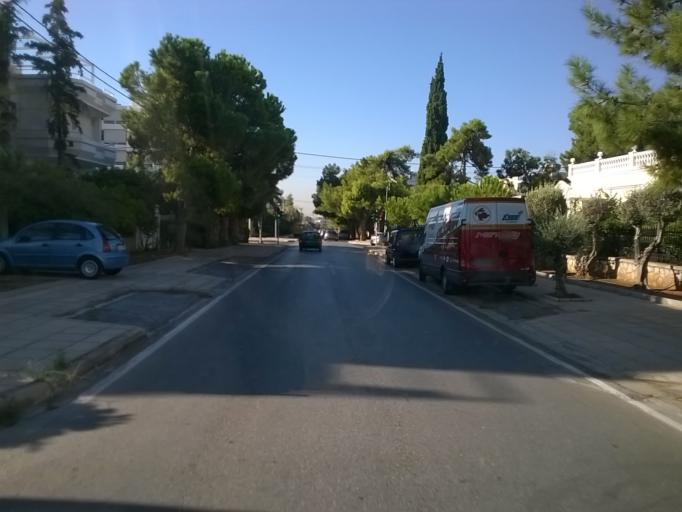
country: GR
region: Attica
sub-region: Nomarchia Athinas
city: Glyfada
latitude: 37.8700
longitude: 23.7541
